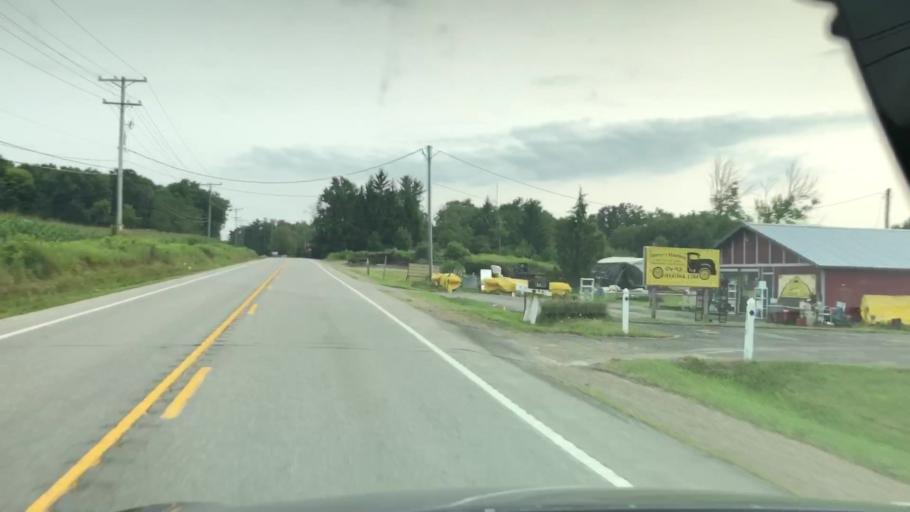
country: US
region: Pennsylvania
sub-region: Crawford County
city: Titusville
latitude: 41.5939
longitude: -79.6824
